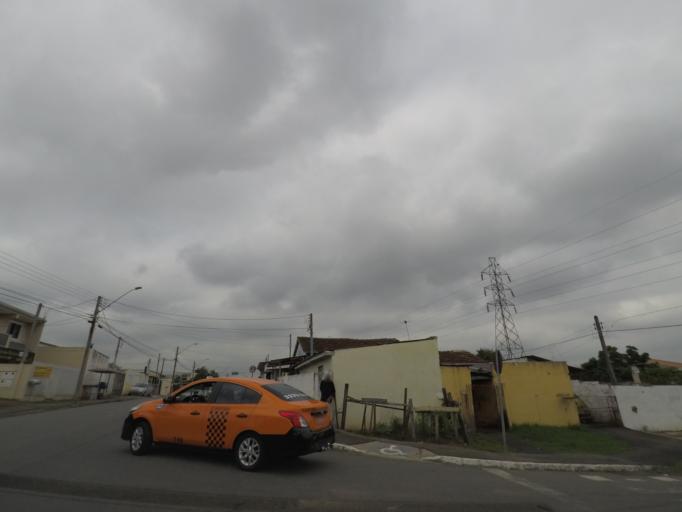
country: BR
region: Parana
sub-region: Curitiba
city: Curitiba
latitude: -25.5163
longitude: -49.3098
